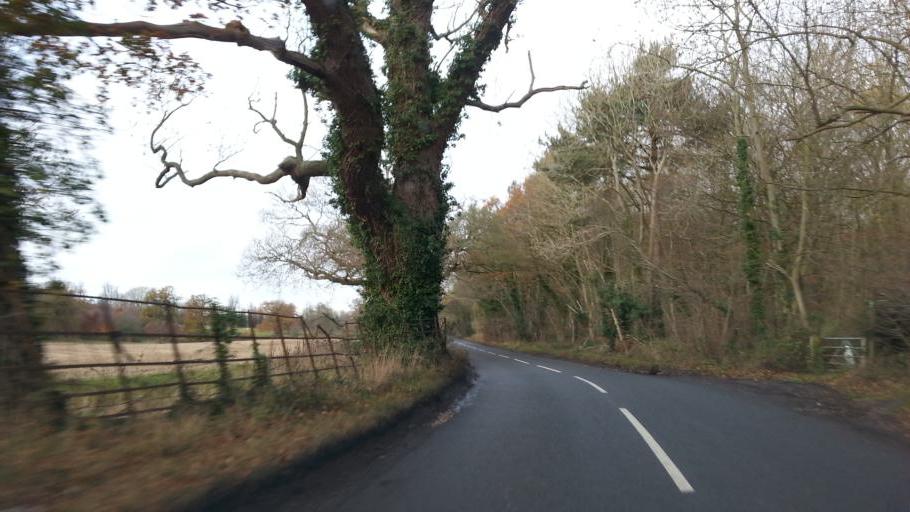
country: GB
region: England
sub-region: Suffolk
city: Wickham Market
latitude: 52.1497
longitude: 1.4261
